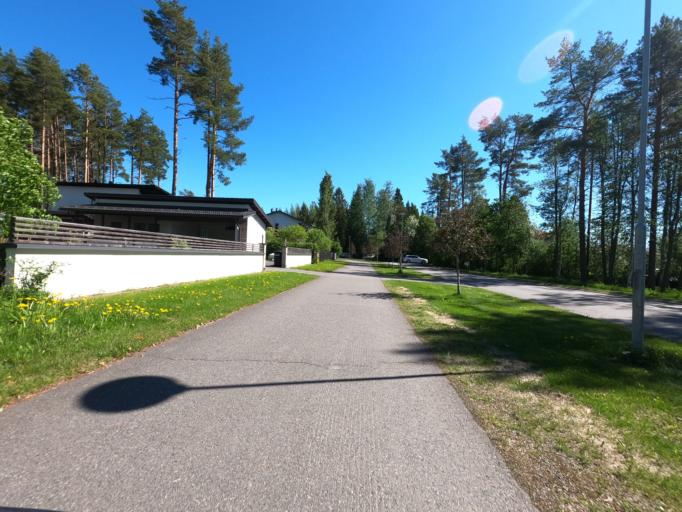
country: FI
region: North Karelia
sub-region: Joensuu
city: Joensuu
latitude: 62.5765
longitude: 29.7682
